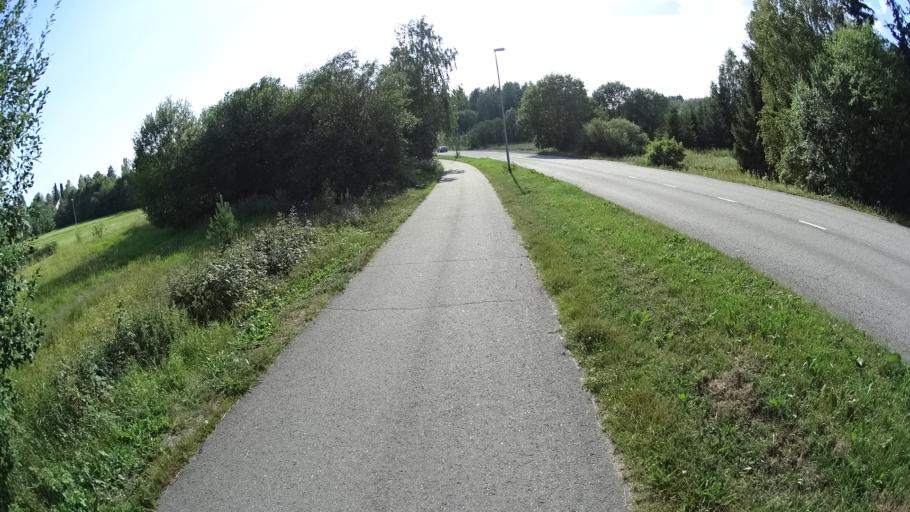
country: FI
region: Uusimaa
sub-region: Porvoo
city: Porvoo
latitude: 60.4135
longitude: 25.6548
